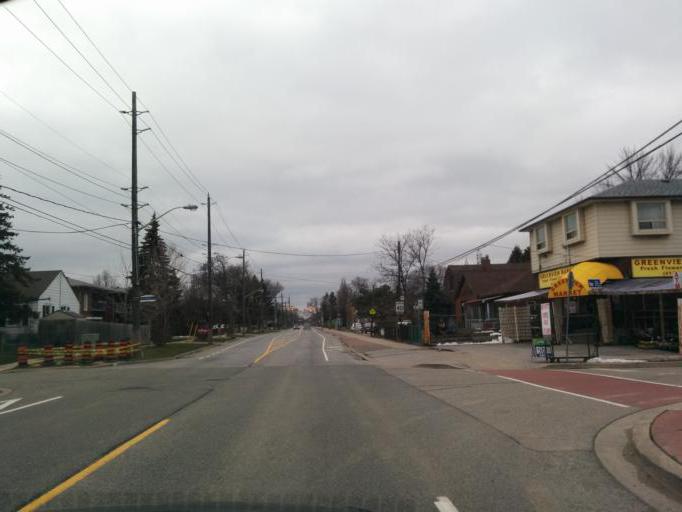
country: CA
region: Ontario
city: Etobicoke
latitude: 43.6293
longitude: -79.5039
